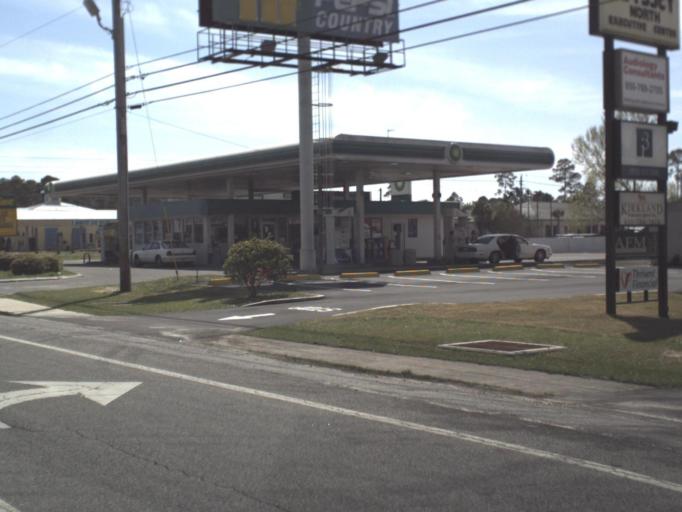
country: US
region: Florida
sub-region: Bay County
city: Lynn Haven
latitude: 30.2195
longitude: -85.6495
